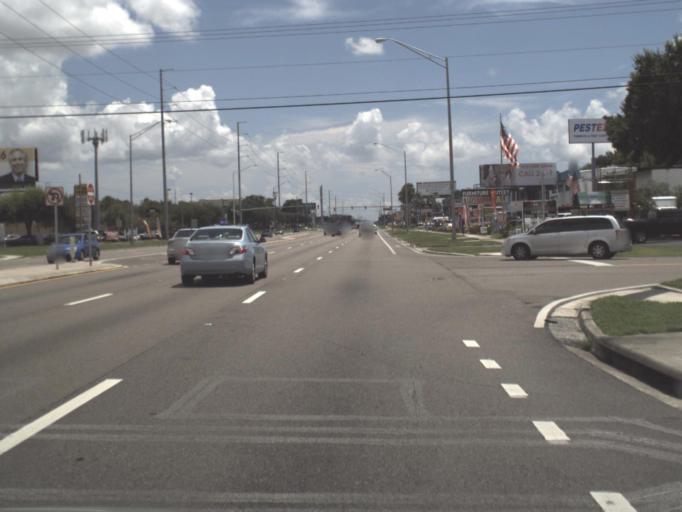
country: US
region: Florida
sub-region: Hillsborough County
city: Egypt Lake-Leto
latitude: 28.0168
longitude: -82.5051
